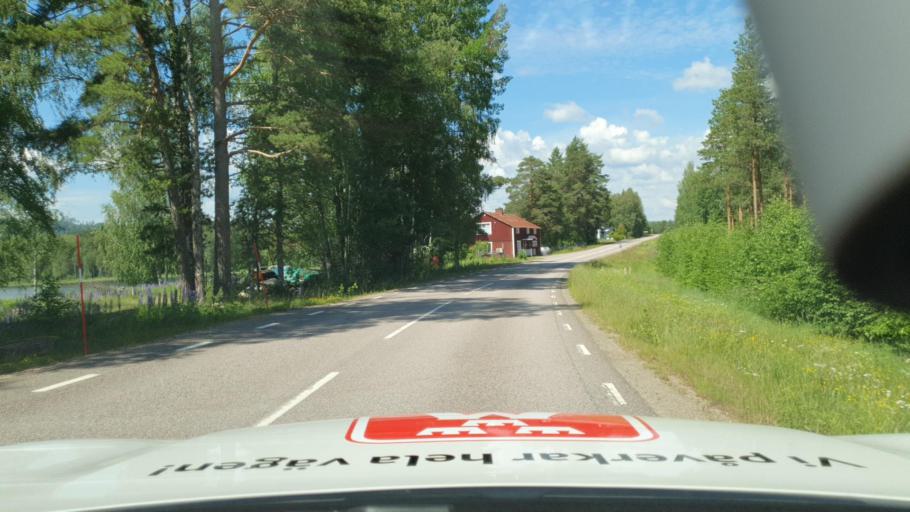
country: SE
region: Vaermland
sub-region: Torsby Kommun
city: Torsby
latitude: 60.3541
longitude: 12.9571
